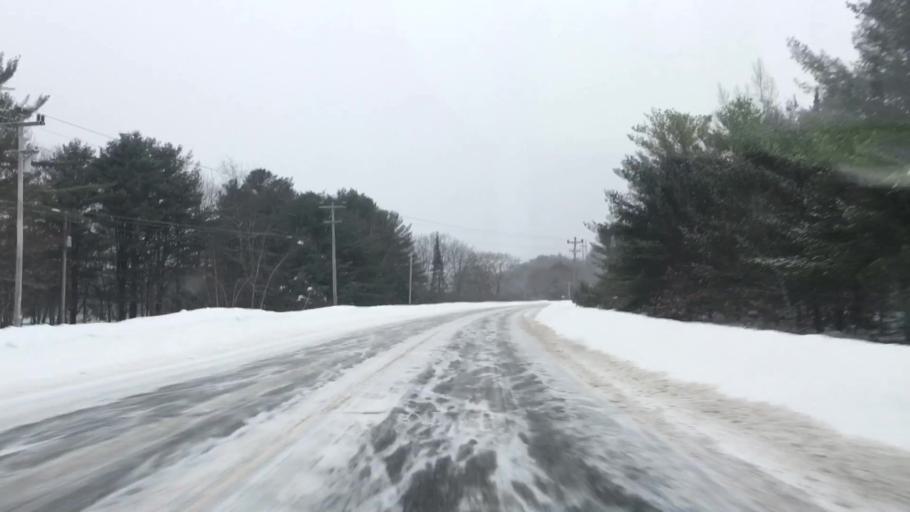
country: US
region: Maine
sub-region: Penobscot County
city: Medway
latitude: 45.5652
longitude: -68.3999
